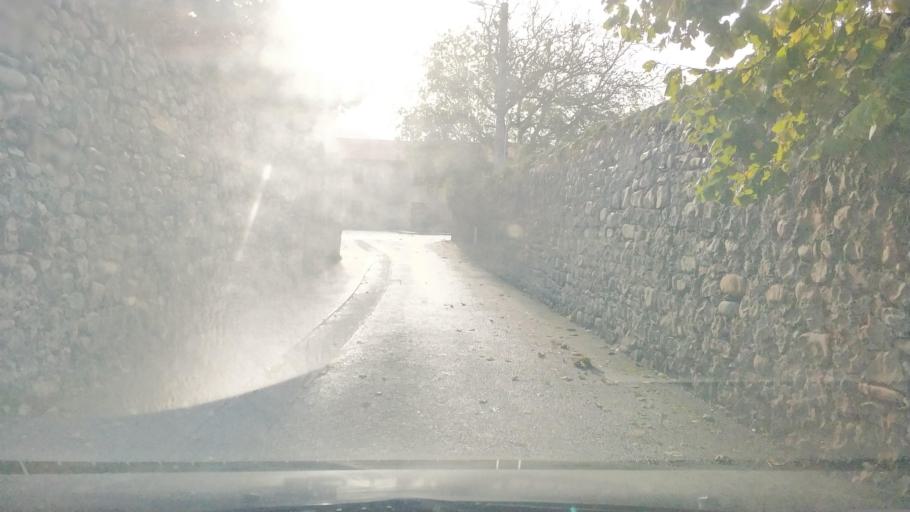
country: ES
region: Cantabria
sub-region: Provincia de Cantabria
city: Luzmela
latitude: 43.3364
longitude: -4.1794
